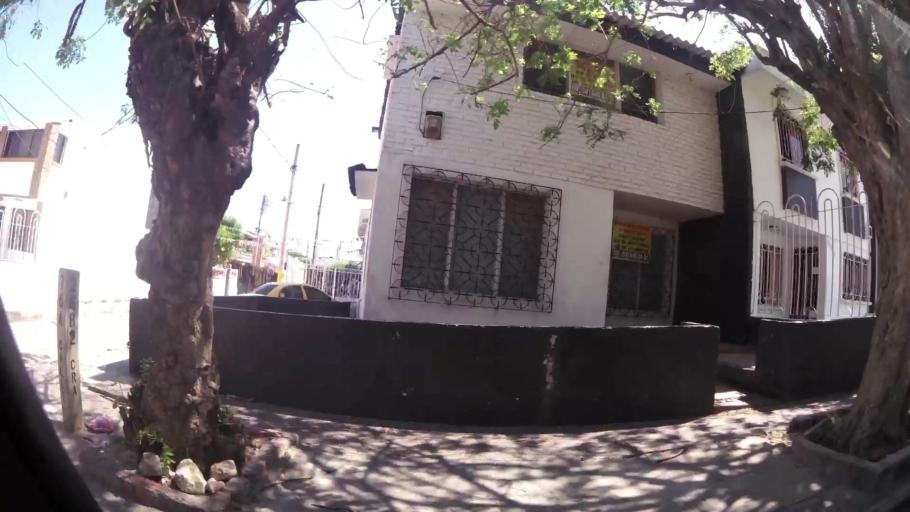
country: CO
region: Atlantico
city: Barranquilla
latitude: 10.9781
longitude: -74.8182
